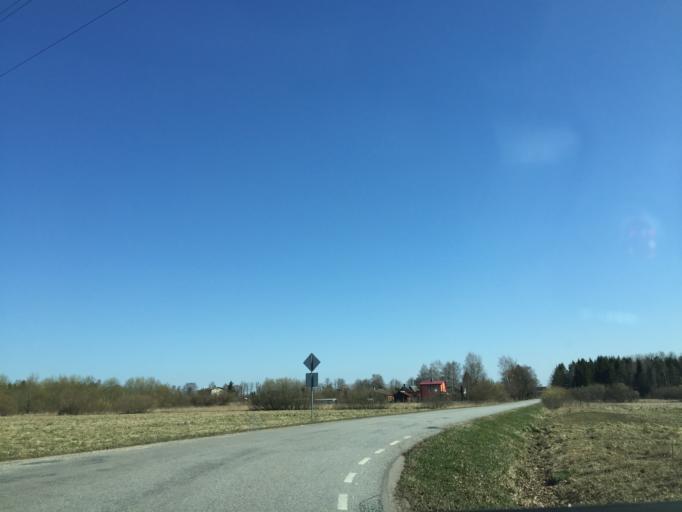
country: EE
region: Tartu
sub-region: Puhja vald
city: Puhja
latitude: 58.3603
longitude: 26.4265
